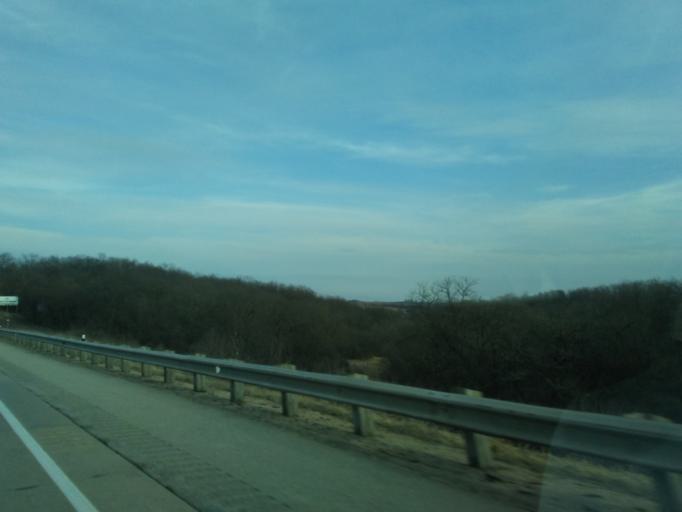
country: US
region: Wisconsin
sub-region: Iowa County
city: Barneveld
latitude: 42.9954
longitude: -89.9901
